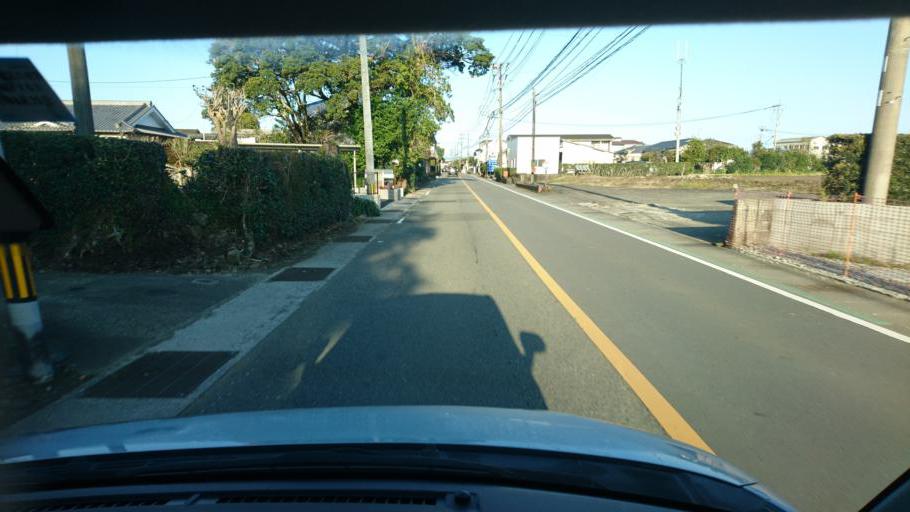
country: JP
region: Miyazaki
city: Miyazaki-shi
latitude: 31.8408
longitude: 131.4194
